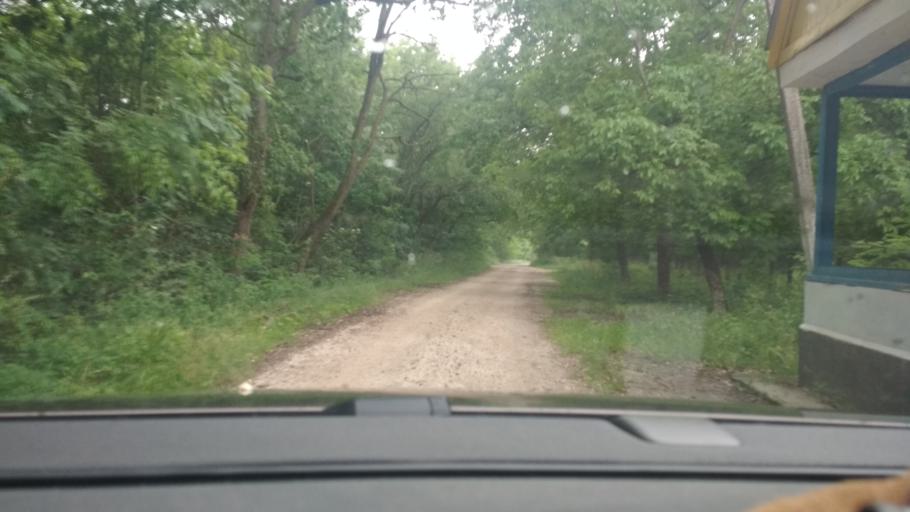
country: MD
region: Singerei
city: Biruinta
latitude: 47.7492
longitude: 28.1398
